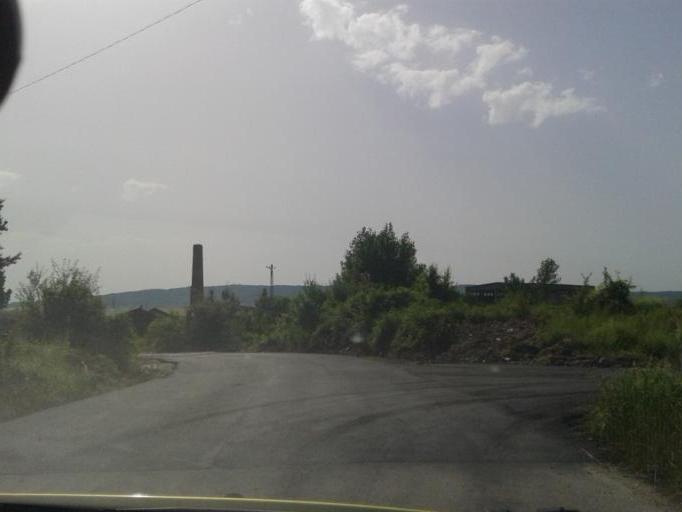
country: RO
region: Valcea
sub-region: Municipiul Ramnicu Valcea
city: Copacelu
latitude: 45.0664
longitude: 24.3334
